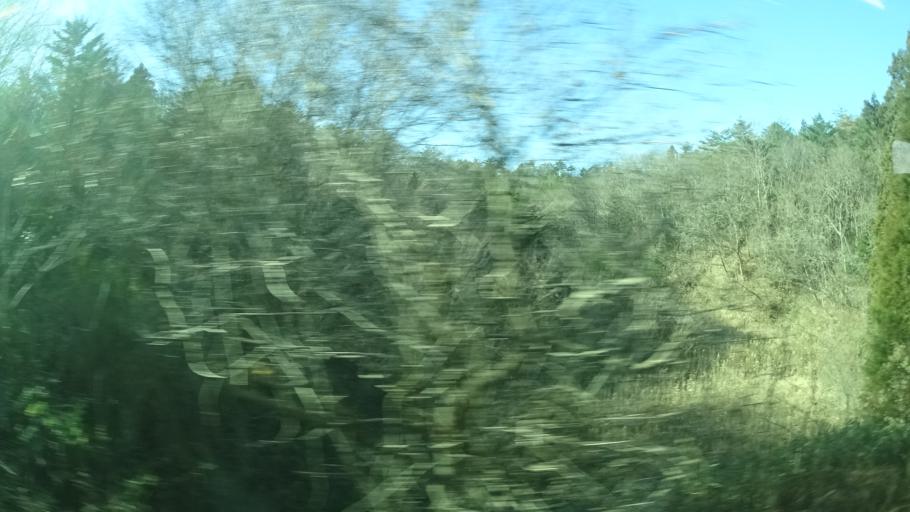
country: JP
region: Fukushima
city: Namie
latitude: 37.6751
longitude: 140.9722
